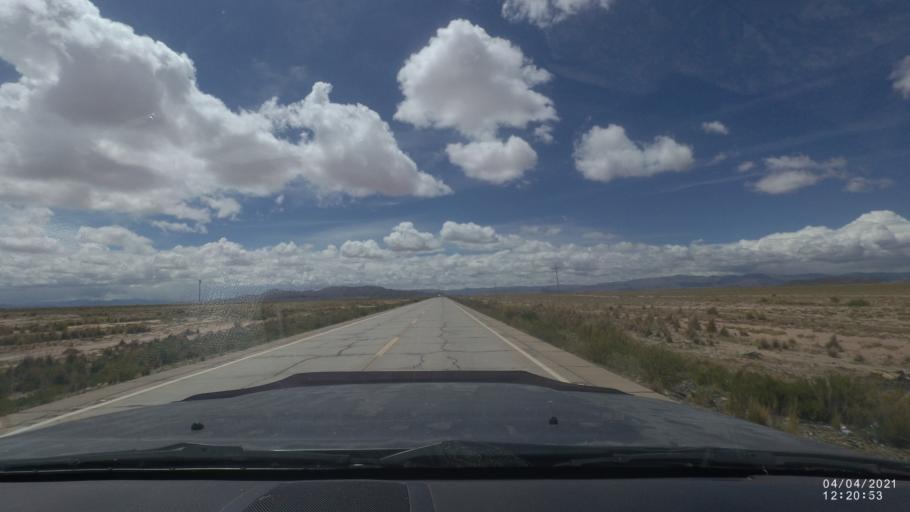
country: BO
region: Oruro
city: Oruro
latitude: -18.0728
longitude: -67.2259
